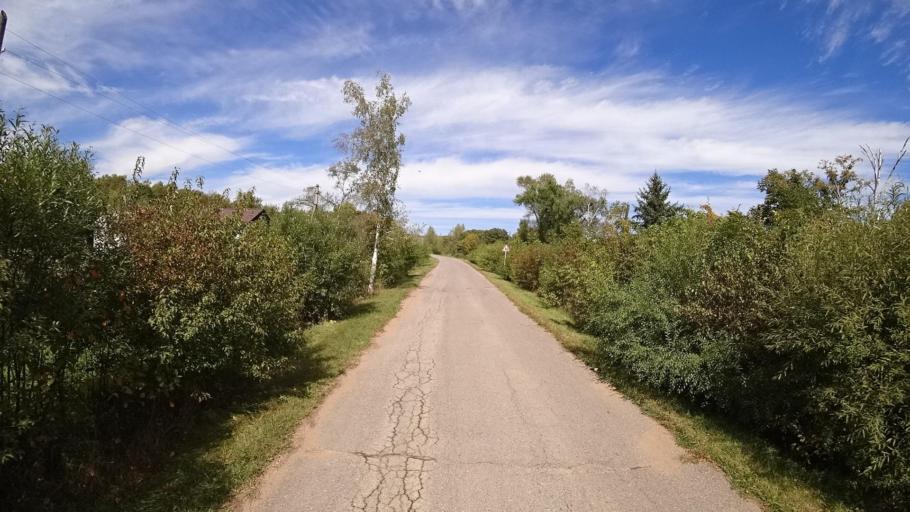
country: RU
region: Primorskiy
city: Yakovlevka
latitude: 44.6507
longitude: 133.5974
